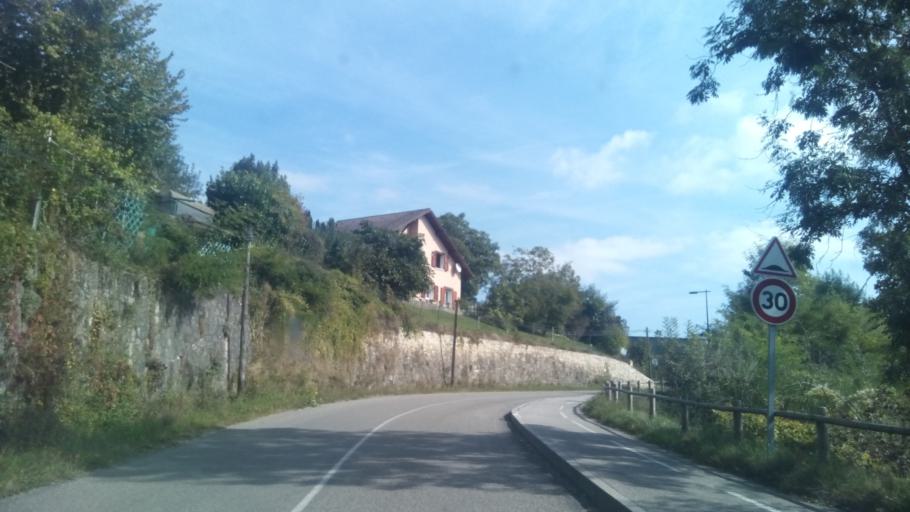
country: FR
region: Rhone-Alpes
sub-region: Departement de la Savoie
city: Le Pont-de-Beauvoisin
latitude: 45.5364
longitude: 5.6798
